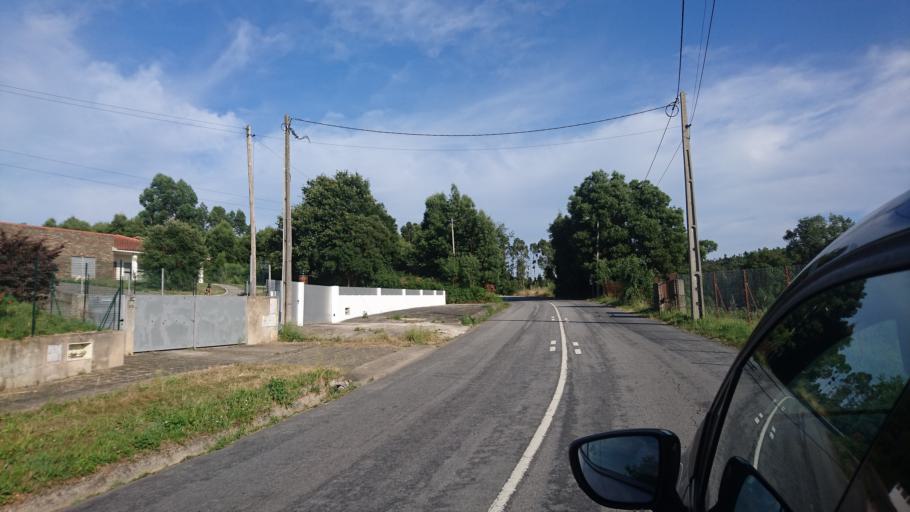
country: PT
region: Porto
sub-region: Paredes
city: Recarei
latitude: 41.1398
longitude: -8.3881
